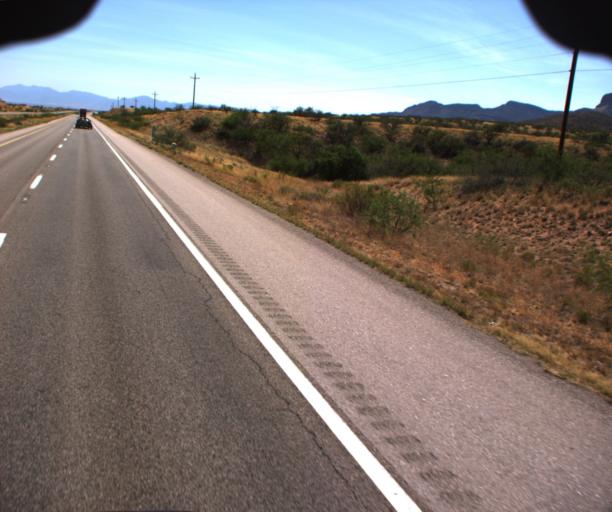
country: US
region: Arizona
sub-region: Cochise County
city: Whetstone
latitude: 31.8574
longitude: -110.3413
